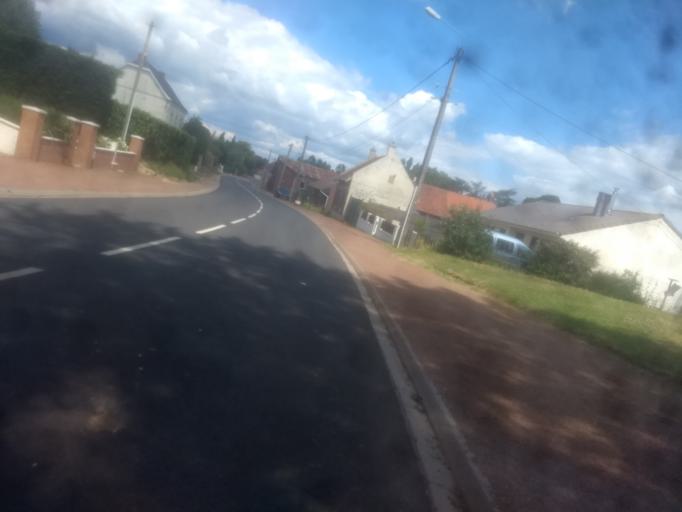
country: FR
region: Nord-Pas-de-Calais
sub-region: Departement du Pas-de-Calais
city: Croisilles
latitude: 50.2216
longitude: 2.8297
